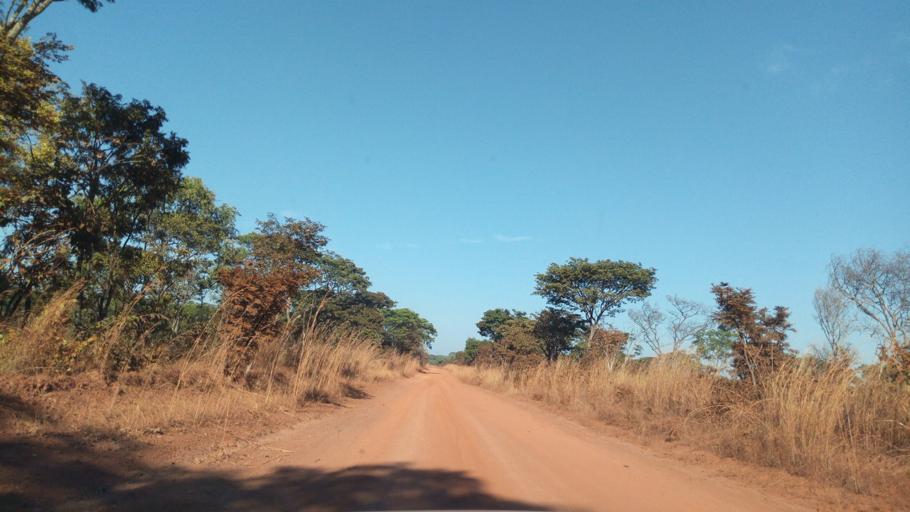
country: ZM
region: Luapula
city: Mwense
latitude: -10.6059
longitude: 28.4184
